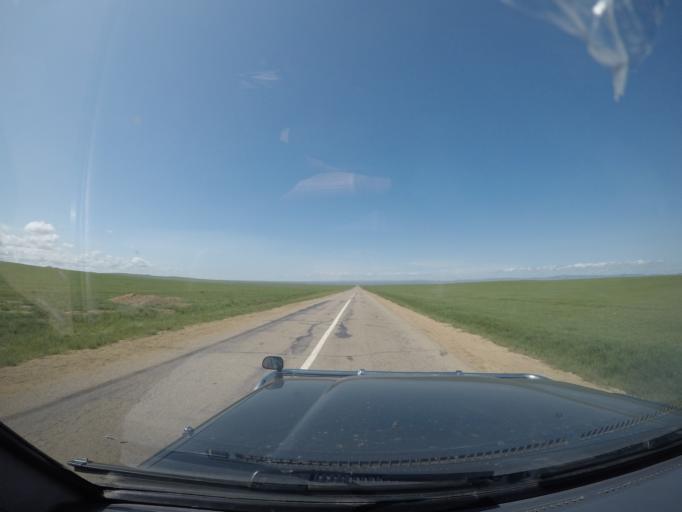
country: MN
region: Hentiy
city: Bayan
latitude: 47.2799
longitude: 110.8483
